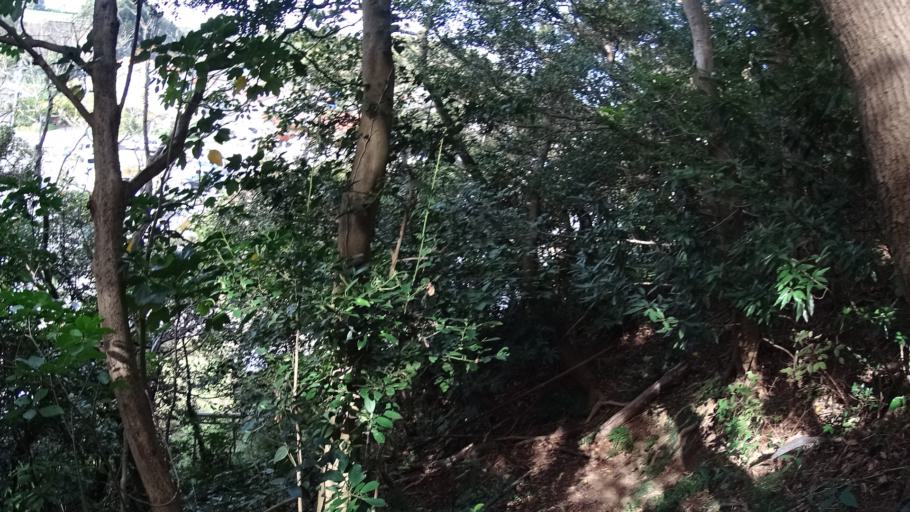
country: JP
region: Kanagawa
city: Miura
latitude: 35.1457
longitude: 139.6781
